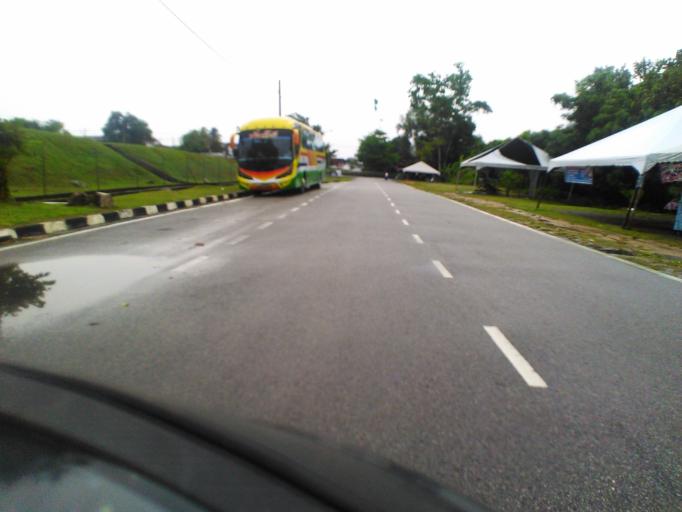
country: MY
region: Kedah
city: Kulim
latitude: 5.3662
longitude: 100.5738
